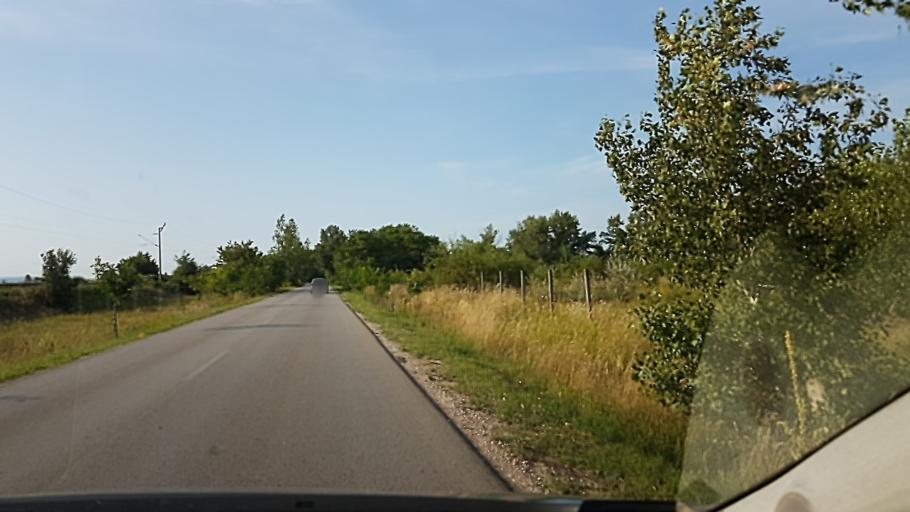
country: HU
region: Pest
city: Dunavarsany
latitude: 47.2613
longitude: 19.0628
